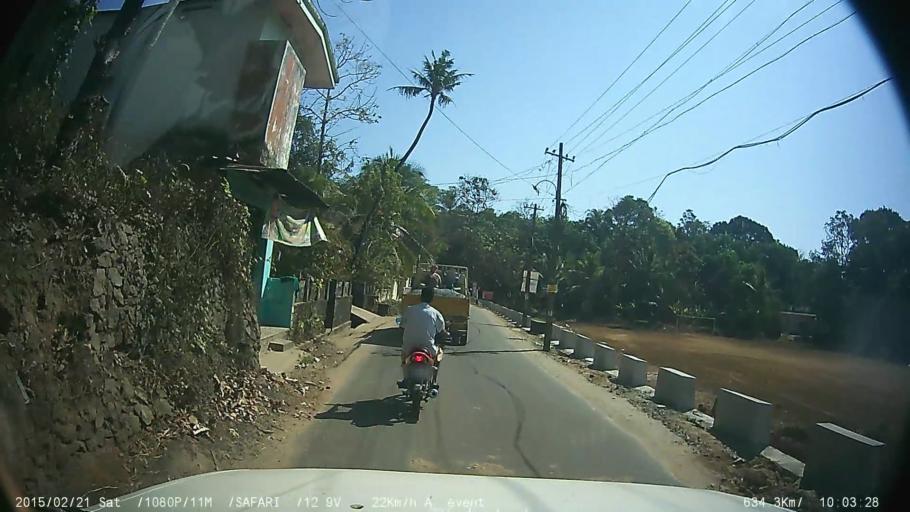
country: IN
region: Kerala
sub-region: Ernakulam
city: Piravam
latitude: 9.8602
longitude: 76.5985
